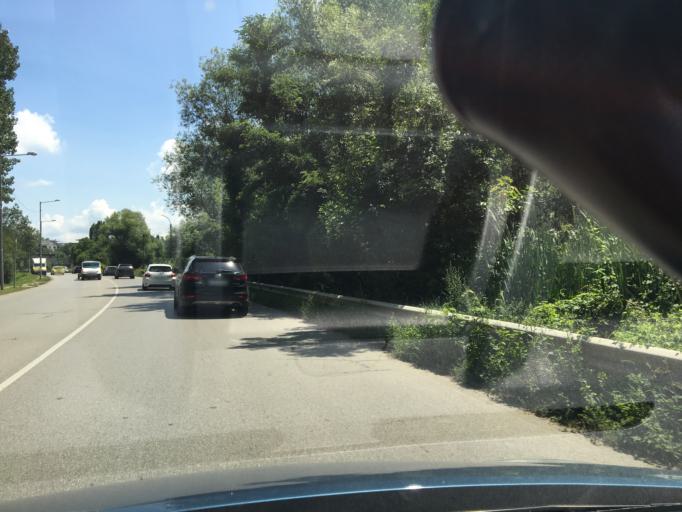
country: BG
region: Sofia-Capital
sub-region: Stolichna Obshtina
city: Sofia
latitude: 42.6583
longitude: 23.3071
